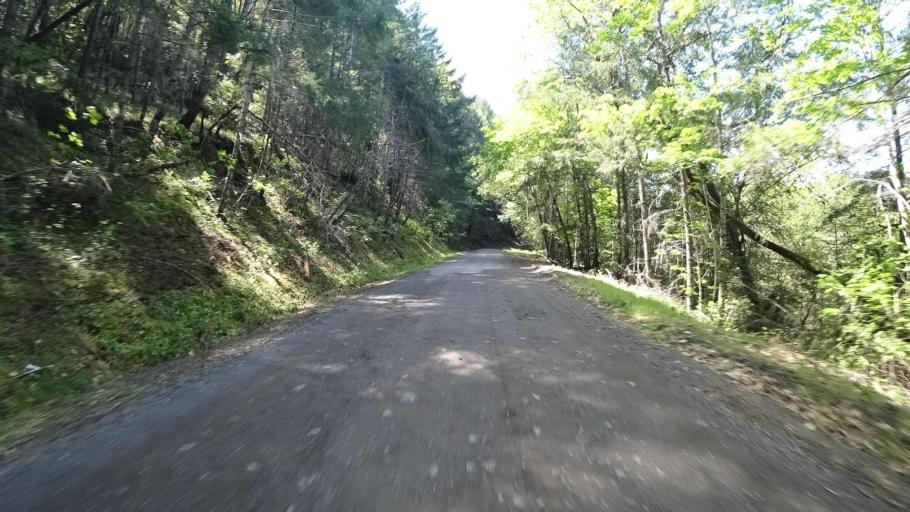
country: US
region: California
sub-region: Humboldt County
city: Redway
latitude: 40.2324
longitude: -123.6433
